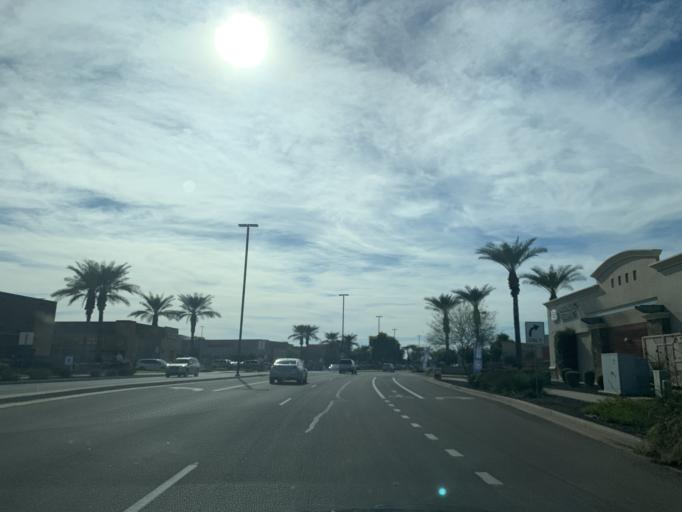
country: US
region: Arizona
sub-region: Maricopa County
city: Gilbert
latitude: 33.3011
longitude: -111.7438
